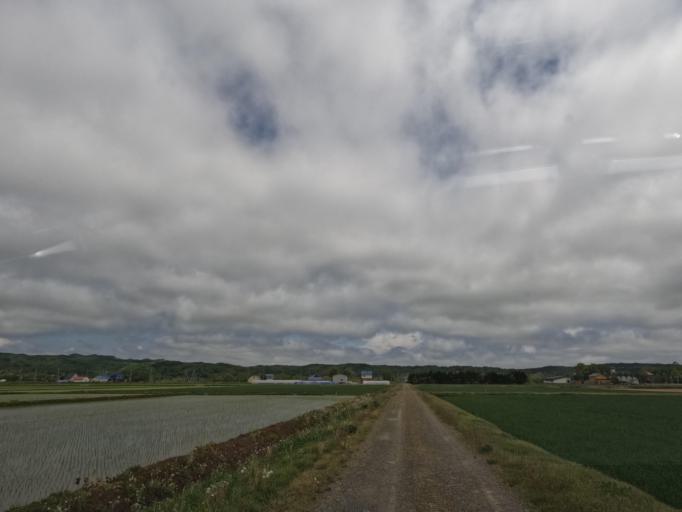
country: JP
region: Hokkaido
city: Tobetsu
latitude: 43.2666
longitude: 141.5237
